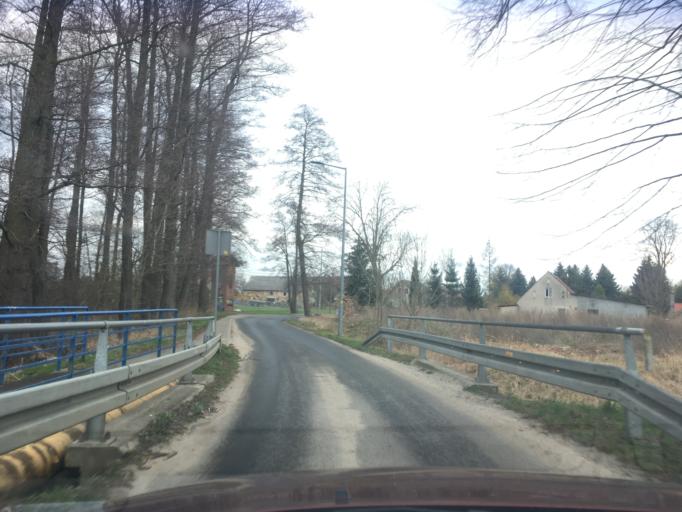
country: PL
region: Lower Silesian Voivodeship
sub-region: Powiat zgorzelecki
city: Lagow
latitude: 51.1491
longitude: 15.0442
